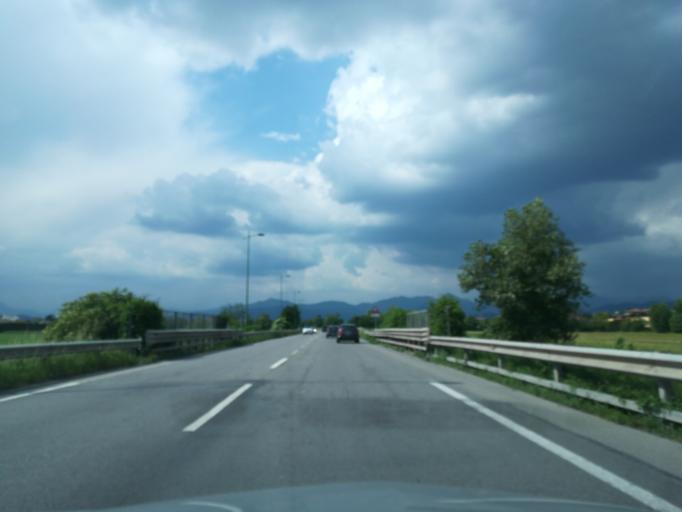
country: IT
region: Lombardy
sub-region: Provincia di Bergamo
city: Grassobbio
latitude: 45.6463
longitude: 9.7450
